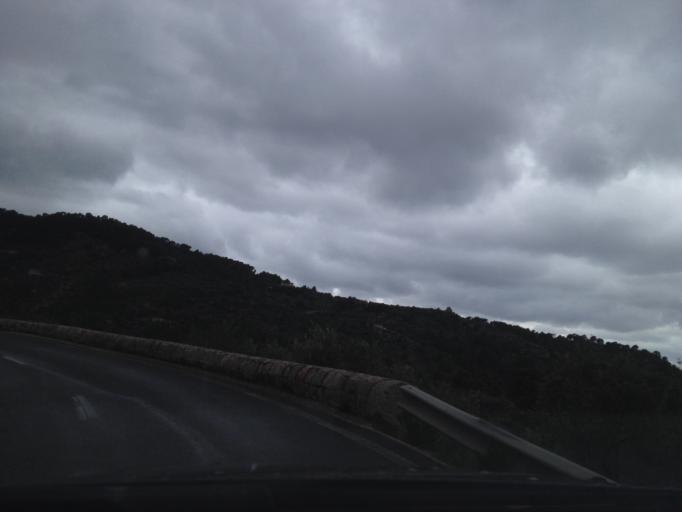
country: ES
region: Balearic Islands
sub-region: Illes Balears
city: Deia
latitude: 39.7580
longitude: 2.6476
